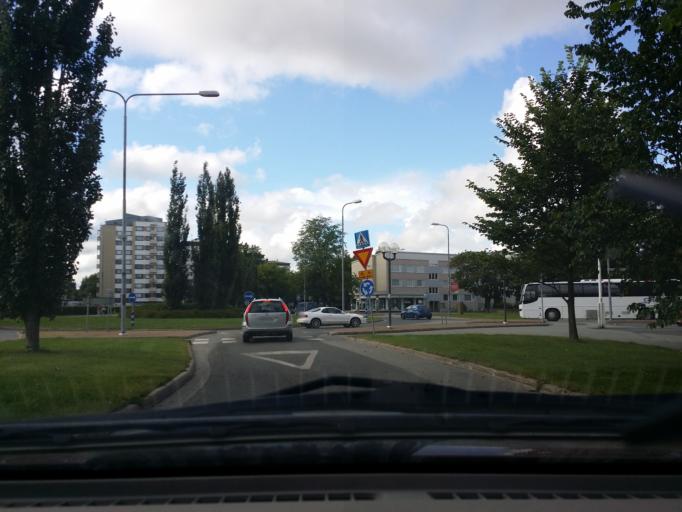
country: FI
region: Satakunta
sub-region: Pori
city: Pori
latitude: 61.4781
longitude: 21.7908
